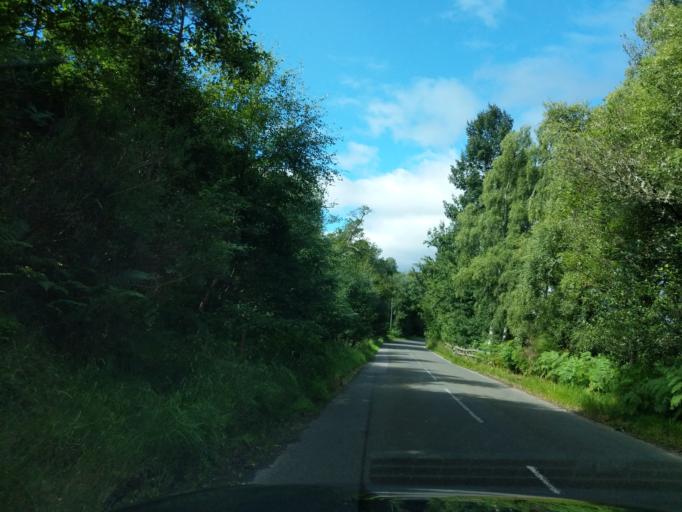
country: GB
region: Scotland
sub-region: Aberdeenshire
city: Aboyne
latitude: 57.0697
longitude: -2.8482
